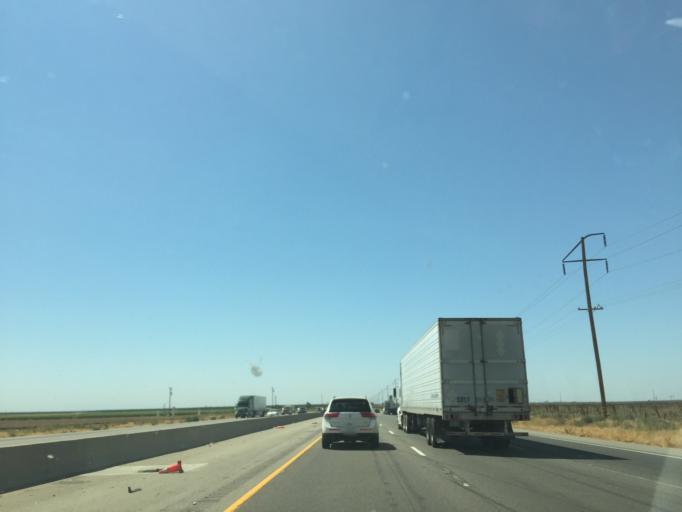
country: US
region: California
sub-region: Kern County
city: Greenacres
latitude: 35.4641
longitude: -119.1171
